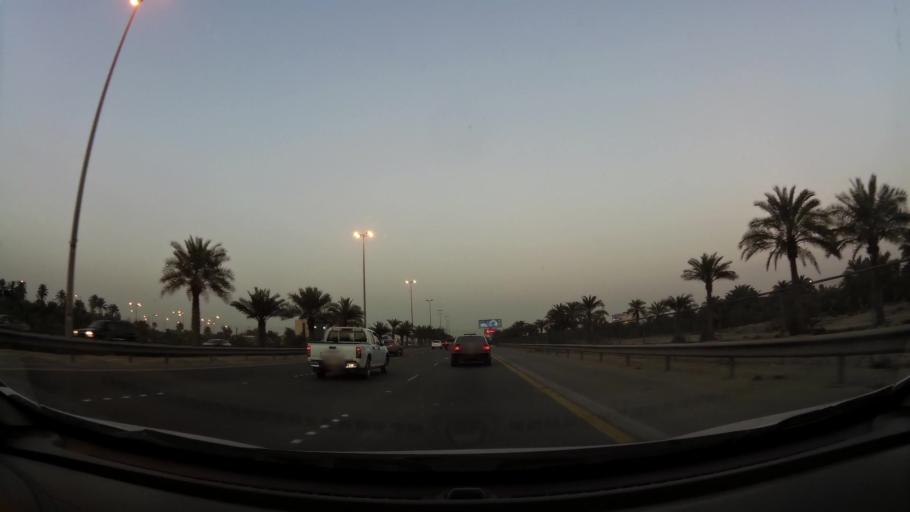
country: BH
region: Manama
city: Jidd Hafs
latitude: 26.1976
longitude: 50.5513
